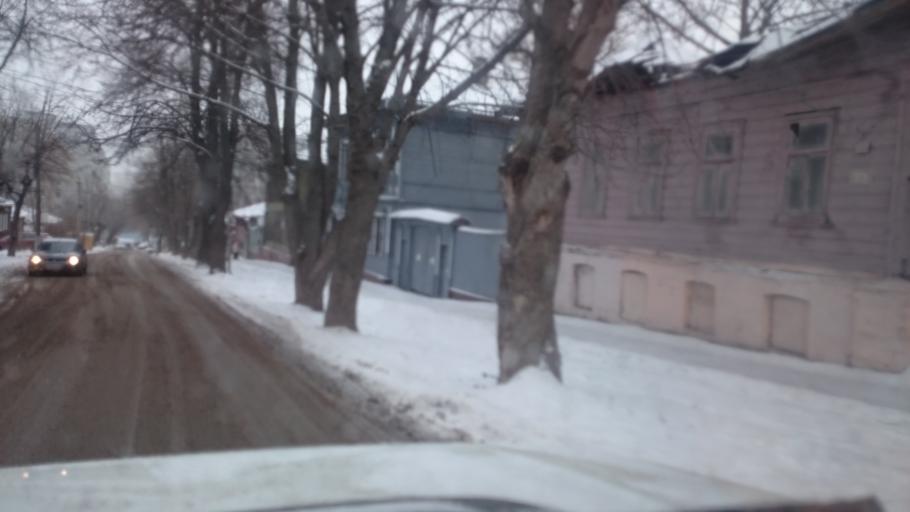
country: RU
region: Tula
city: Tula
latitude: 54.1891
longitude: 37.6028
